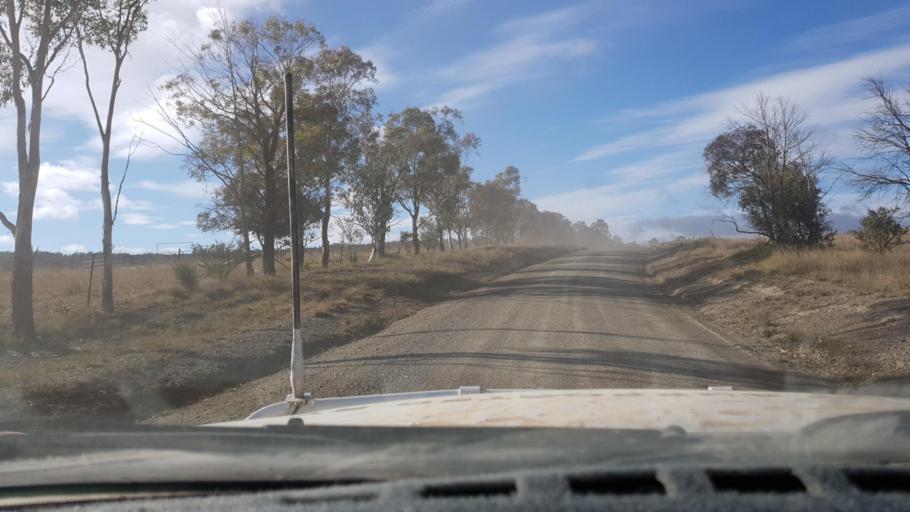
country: AU
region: New South Wales
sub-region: Armidale Dumaresq
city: Enmore
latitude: -30.7467
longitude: 151.6181
